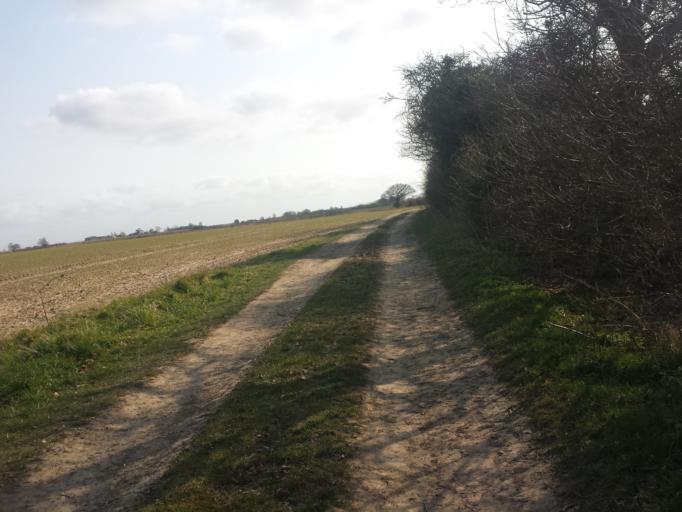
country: GB
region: England
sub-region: Essex
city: Little Clacton
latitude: 51.8966
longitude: 1.1613
